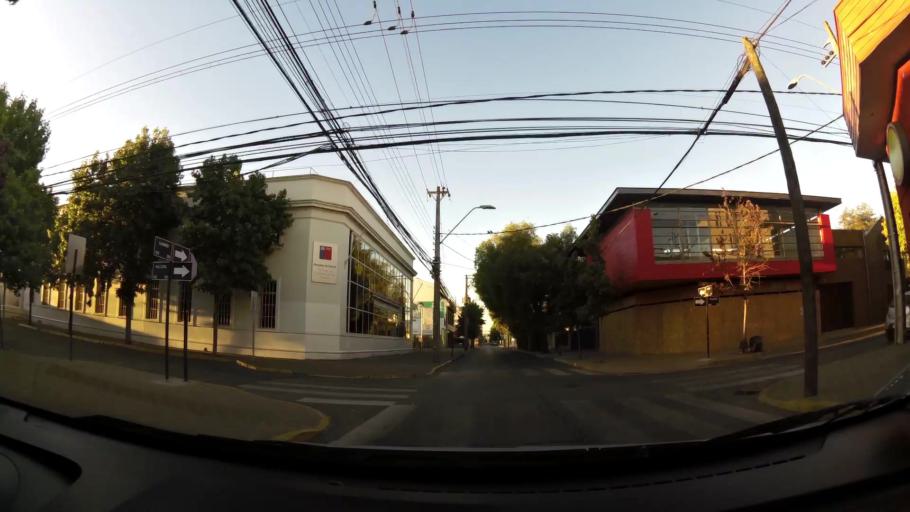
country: CL
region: Maule
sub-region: Provincia de Curico
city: Curico
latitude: -34.9881
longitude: -71.2384
